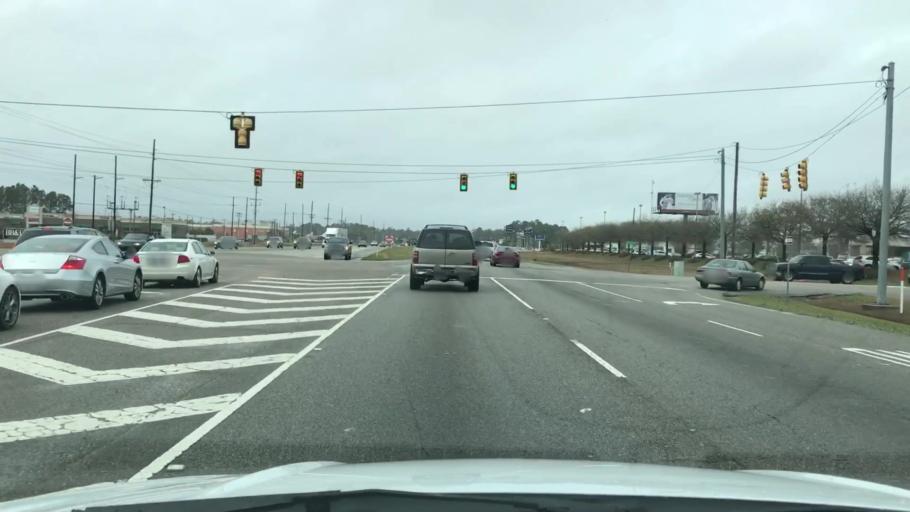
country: US
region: South Carolina
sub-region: Horry County
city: Red Hill
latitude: 33.7904
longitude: -78.9965
